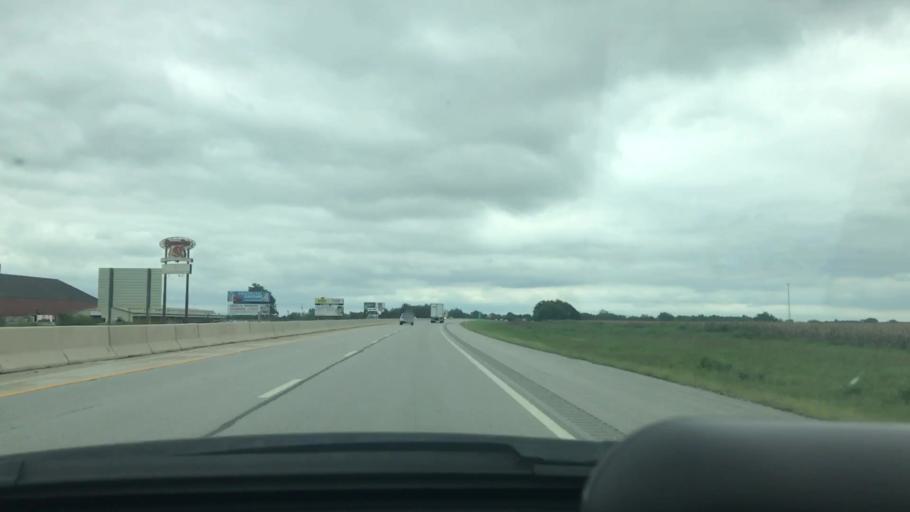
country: US
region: Oklahoma
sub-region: Ottawa County
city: Miami
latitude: 36.8871
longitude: -94.8374
